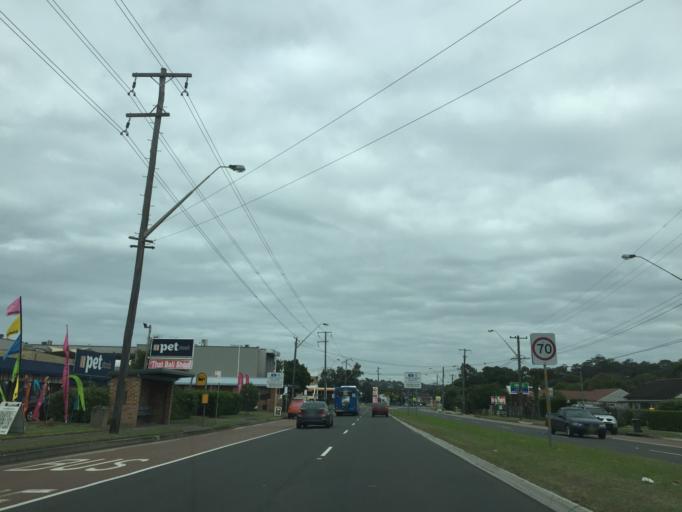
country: AU
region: New South Wales
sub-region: Pittwater
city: Warriewood
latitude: -33.6981
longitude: 151.3006
